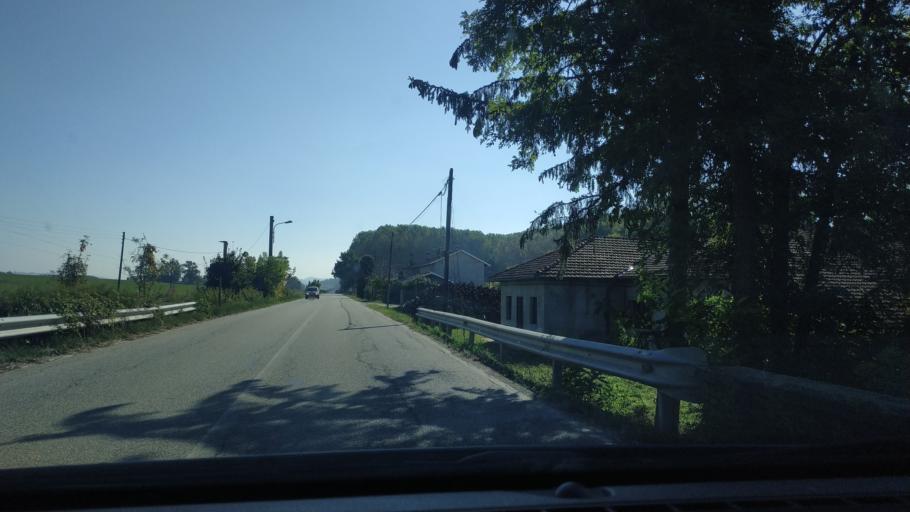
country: IT
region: Piedmont
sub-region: Provincia di Alessandria
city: Serralunga di Crea
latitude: 45.1155
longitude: 8.2650
